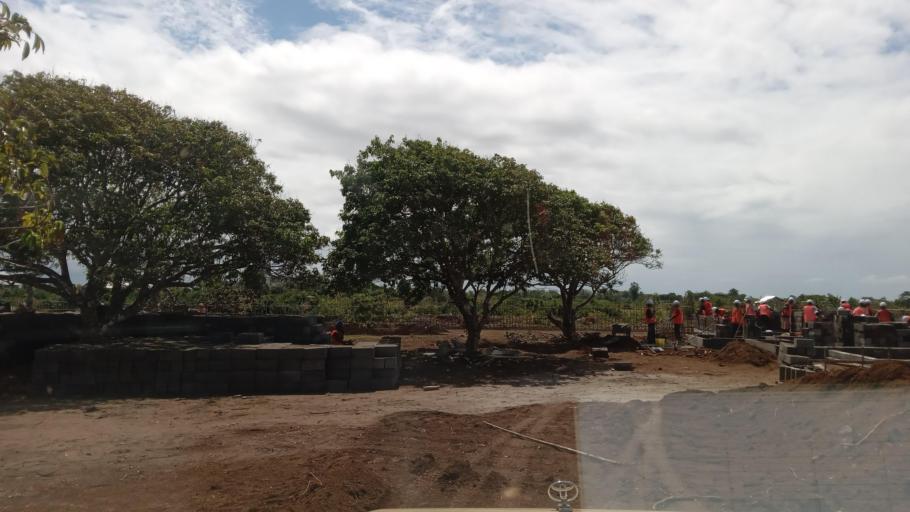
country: MG
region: Atsimo-Atsinanana
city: Vohipaho
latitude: -23.8327
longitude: 47.5539
